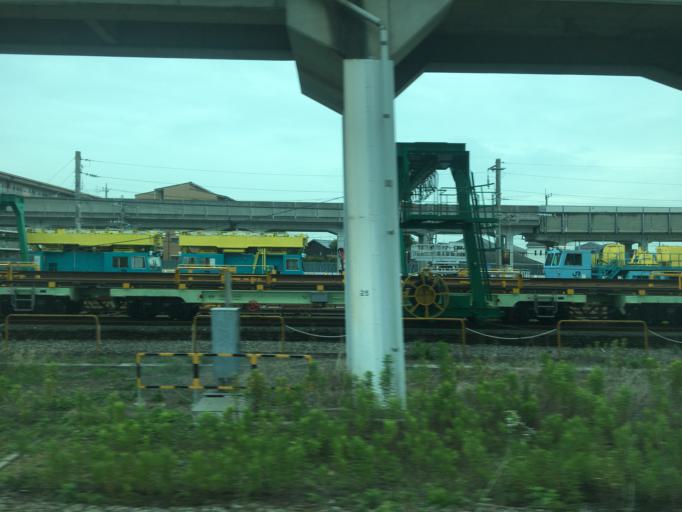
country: JP
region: Saitama
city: Kukichuo
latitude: 36.0860
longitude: 139.6797
